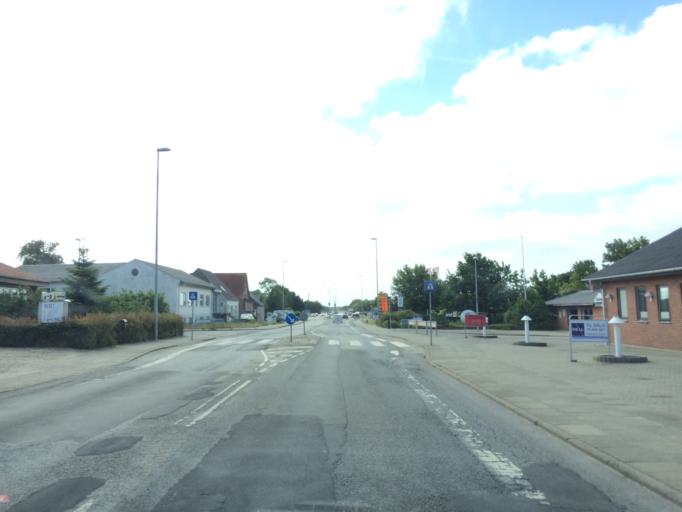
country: DK
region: Central Jutland
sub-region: Herning Kommune
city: Snejbjerg
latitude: 56.1628
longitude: 8.9230
